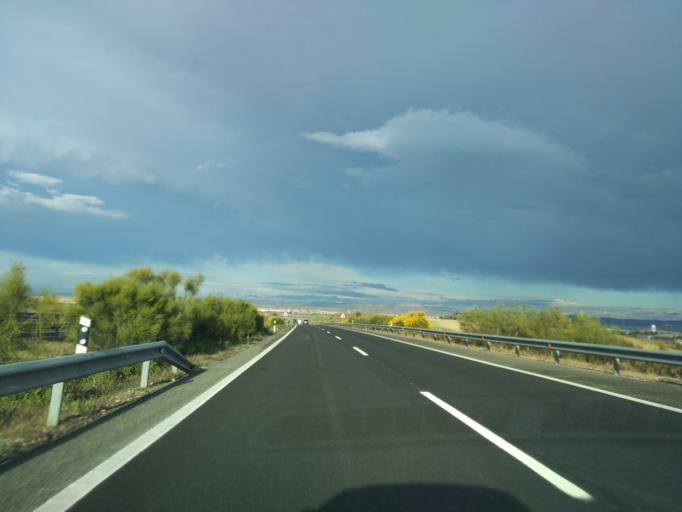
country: ES
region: Madrid
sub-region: Provincia de Madrid
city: Ajalvir
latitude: 40.5060
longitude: -3.4718
